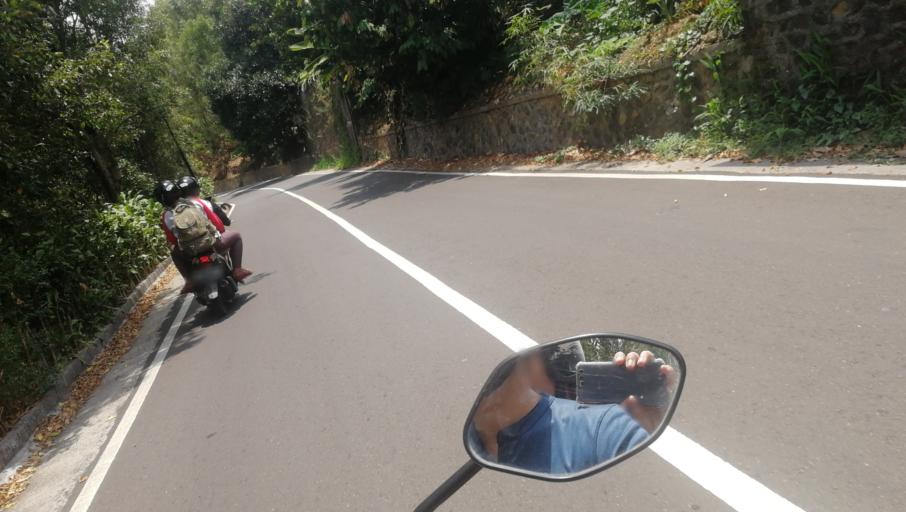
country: ID
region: Bali
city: Banjar Pedawa
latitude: -8.2641
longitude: 115.0453
